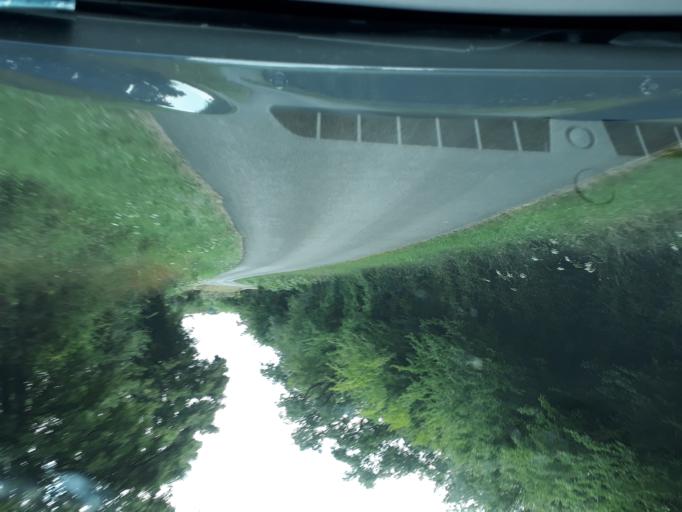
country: FR
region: Centre
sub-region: Departement du Cher
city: Jouet-sur-l'Aubois
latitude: 46.9767
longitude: 2.9412
